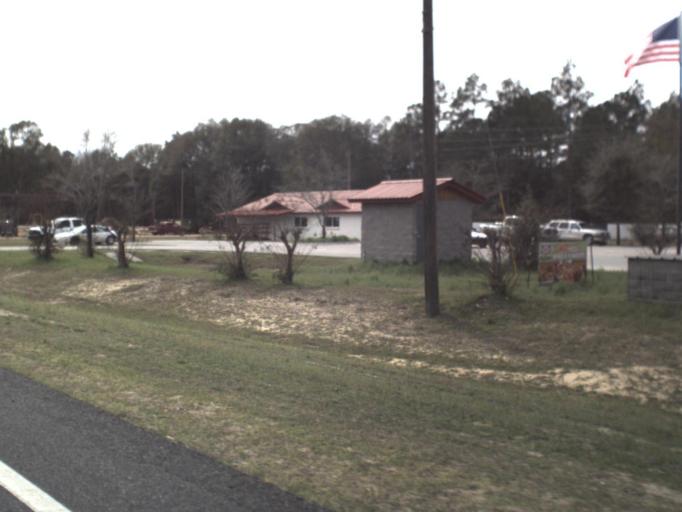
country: US
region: Florida
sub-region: Bay County
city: Youngstown
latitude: 30.4914
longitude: -85.4170
